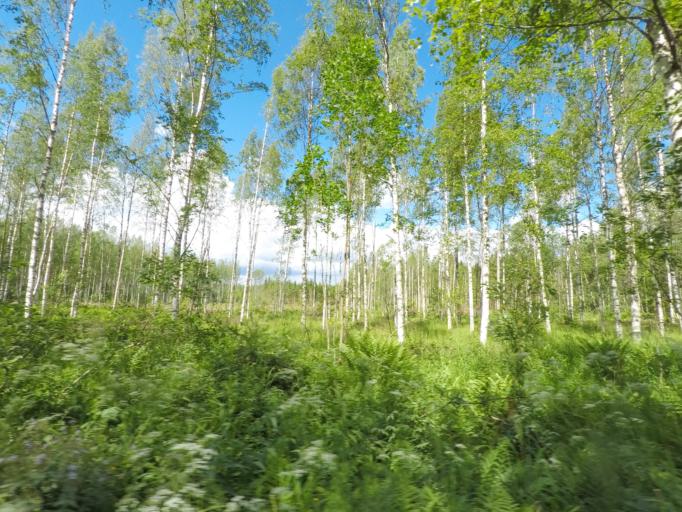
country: FI
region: Central Finland
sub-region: Jyvaeskylae
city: Hankasalmi
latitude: 62.4387
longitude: 26.6457
